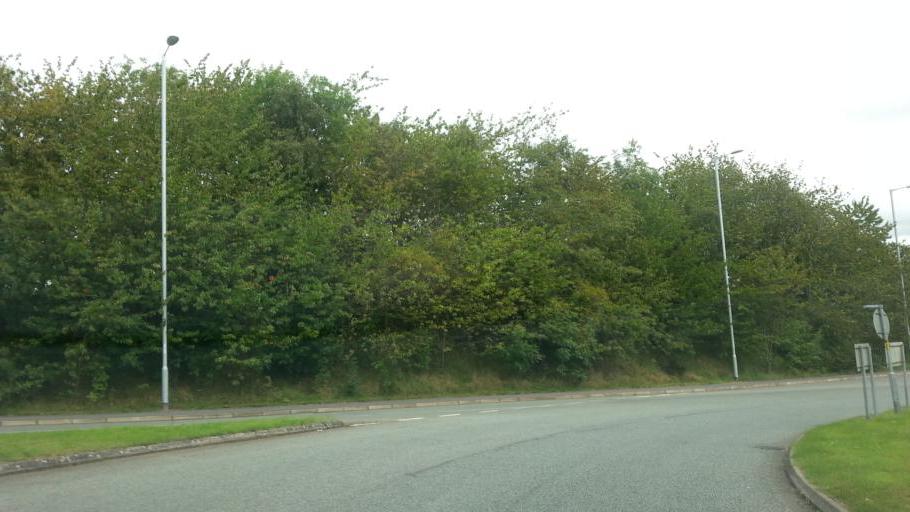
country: GB
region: England
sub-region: Northamptonshire
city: Earls Barton
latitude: 52.2737
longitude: -0.8142
